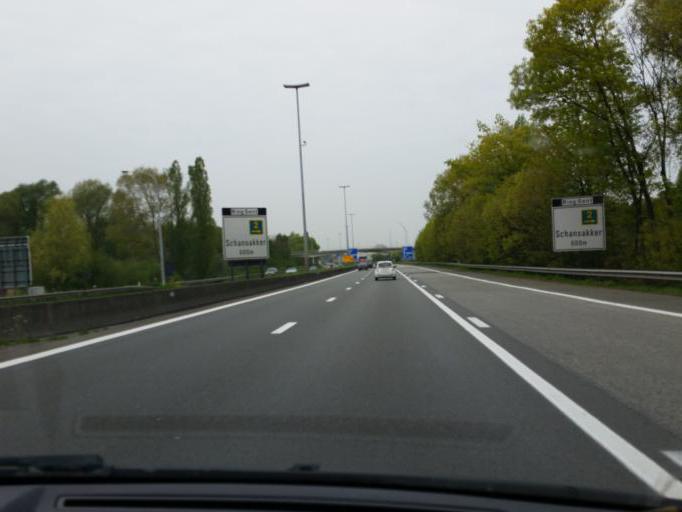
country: BE
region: Flanders
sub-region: Provincie Oost-Vlaanderen
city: Destelbergen
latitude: 51.0845
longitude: 3.7863
